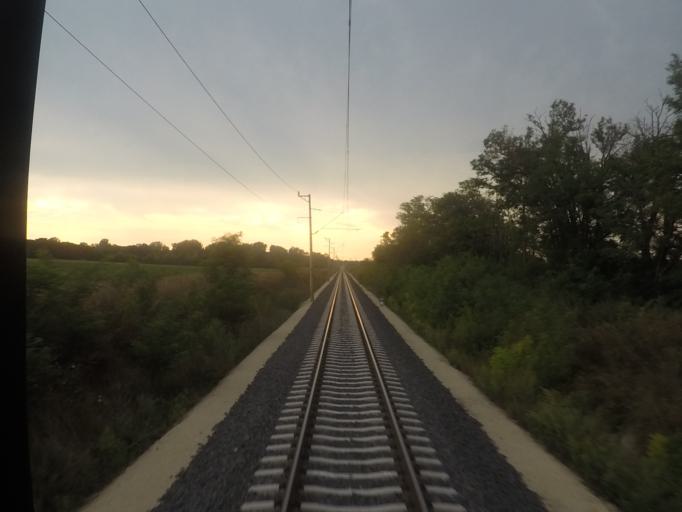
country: HU
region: Fejer
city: Lepseny
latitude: 46.9802
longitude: 18.2043
